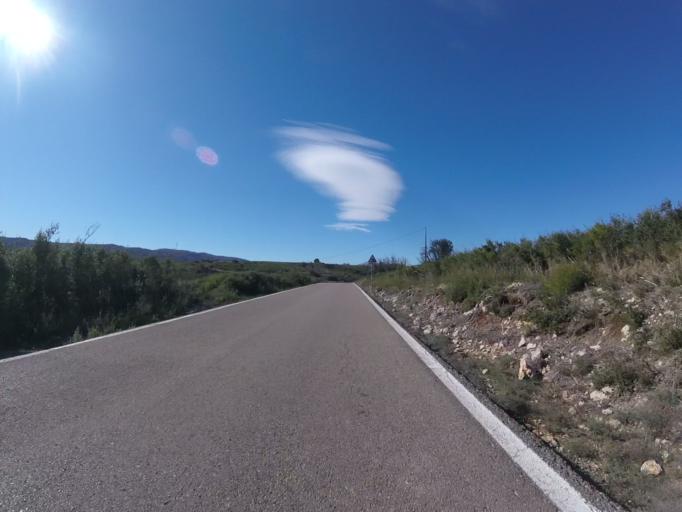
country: ES
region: Valencia
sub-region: Provincia de Castello
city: Albocasser
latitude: 40.3765
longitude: 0.0204
